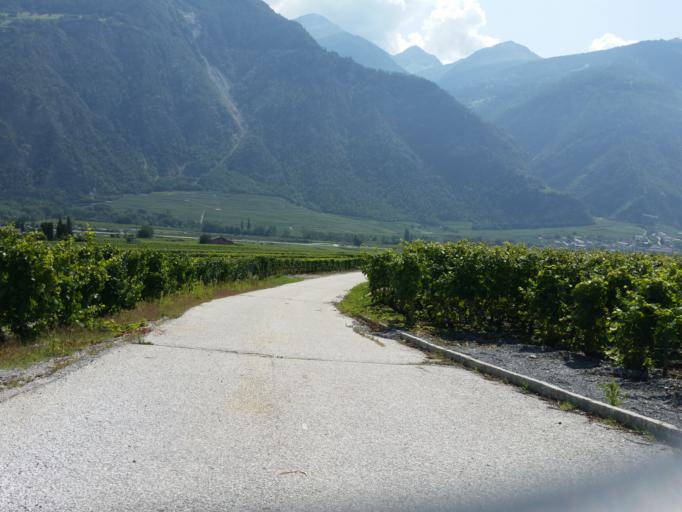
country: CH
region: Valais
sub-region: Conthey District
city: Chamoson
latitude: 46.1943
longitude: 7.2284
